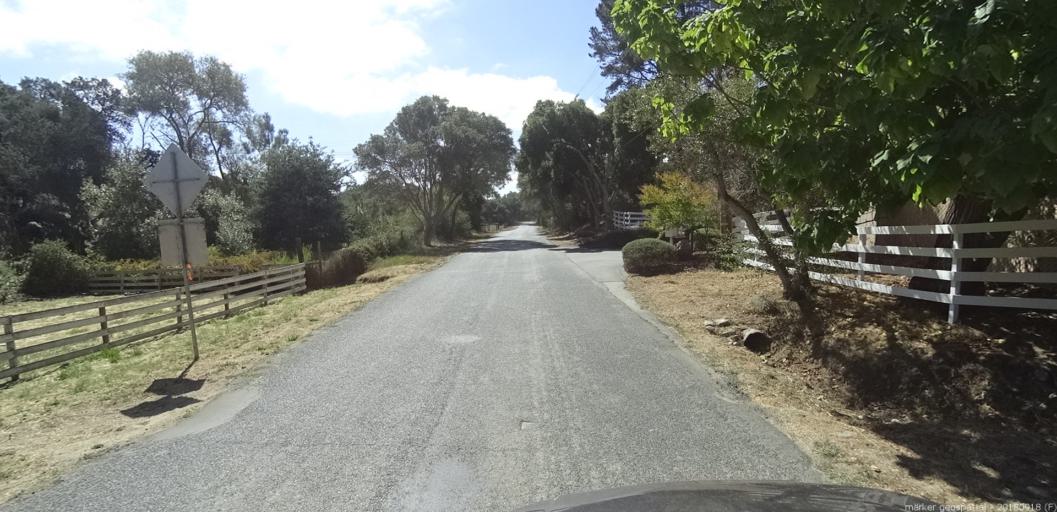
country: US
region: California
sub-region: Monterey County
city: Prunedale
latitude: 36.7864
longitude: -121.6706
